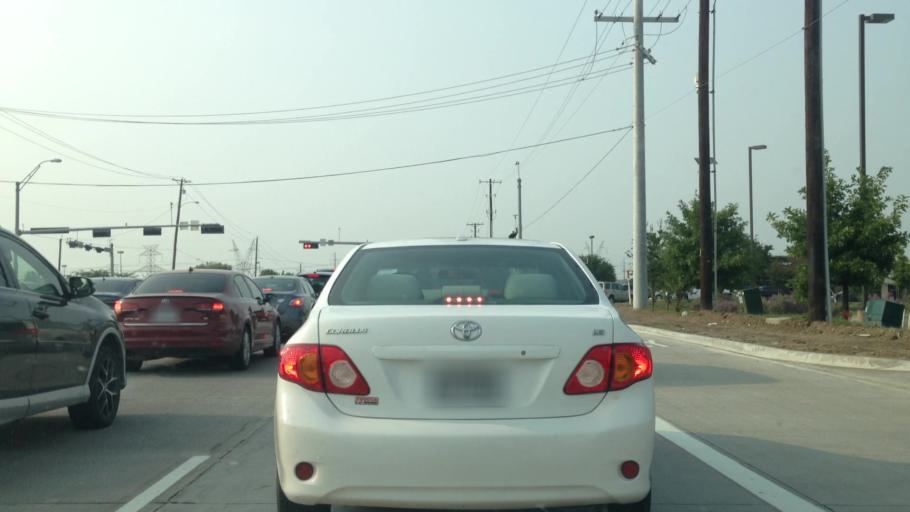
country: US
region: Texas
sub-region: Dallas County
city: Carrollton
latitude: 33.0201
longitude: -96.9154
